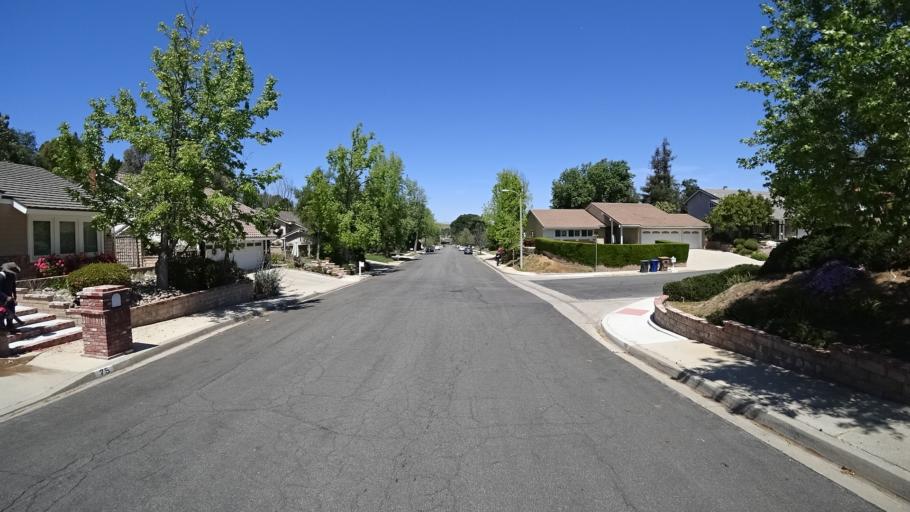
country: US
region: California
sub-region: Ventura County
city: Casa Conejo
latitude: 34.1791
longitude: -118.9030
